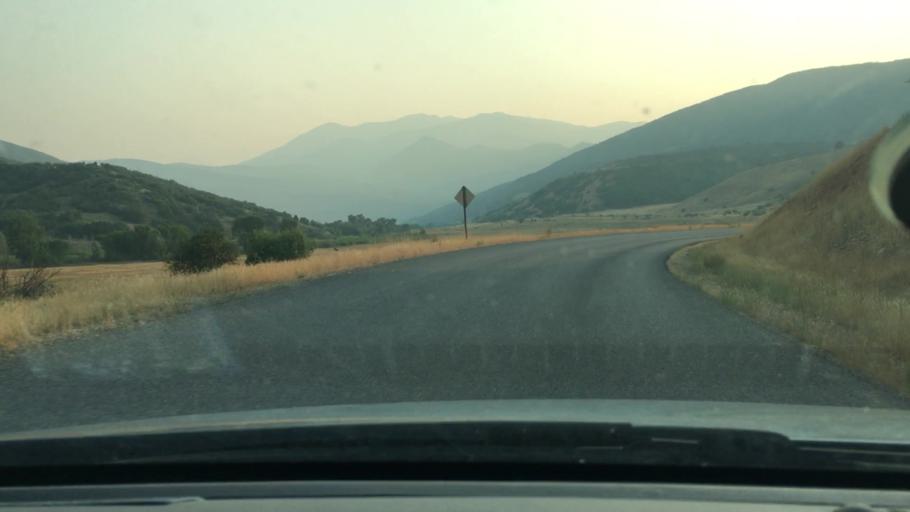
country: US
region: Utah
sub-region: Utah County
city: Mapleton
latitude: 40.0466
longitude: -111.4694
